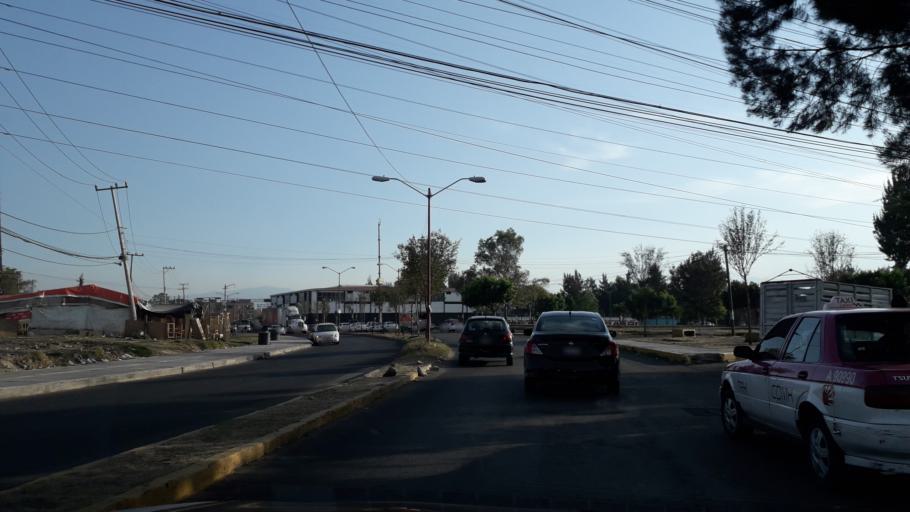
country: MX
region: Mexico City
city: Iztapalapa
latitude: 19.3635
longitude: -99.0486
